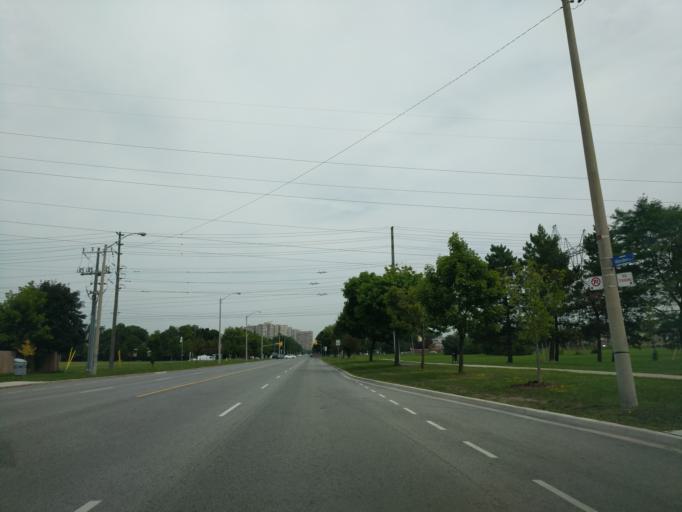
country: CA
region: Ontario
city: Scarborough
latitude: 43.8046
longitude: -79.3201
